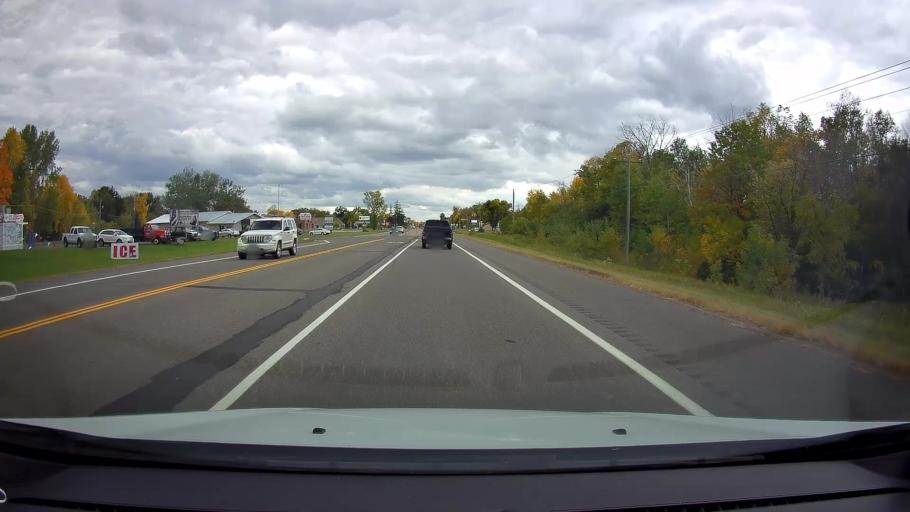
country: US
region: Minnesota
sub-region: Chisago County
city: Chisago City
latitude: 45.3777
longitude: -92.8781
